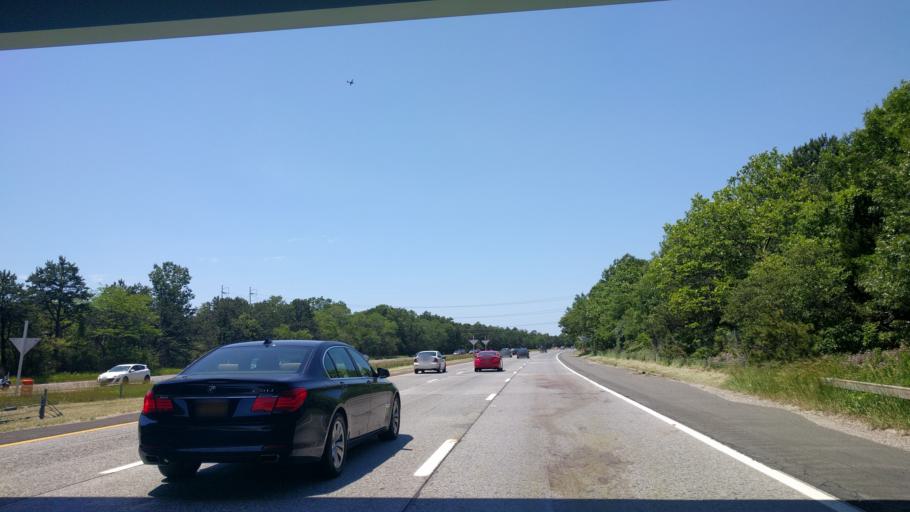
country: US
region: New York
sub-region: Suffolk County
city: Manorville
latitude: 40.8547
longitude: -72.8432
